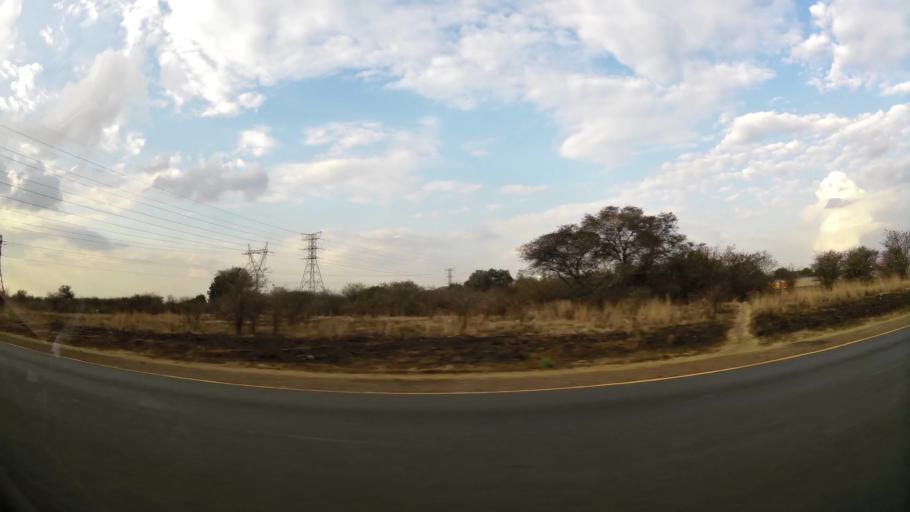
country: ZA
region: Gauteng
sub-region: Sedibeng District Municipality
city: Vanderbijlpark
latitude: -26.6748
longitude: 27.7918
